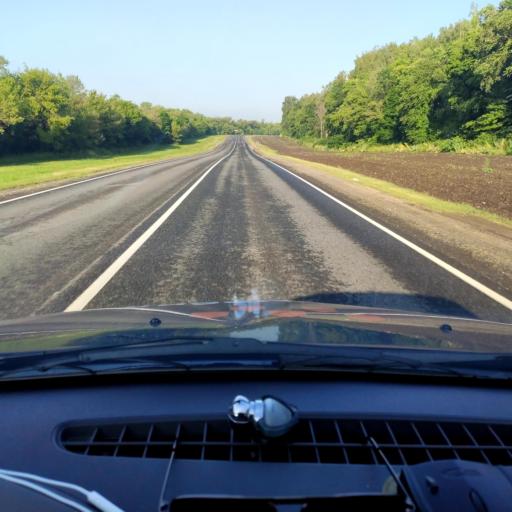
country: RU
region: Orjol
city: Livny
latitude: 52.4311
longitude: 37.8533
